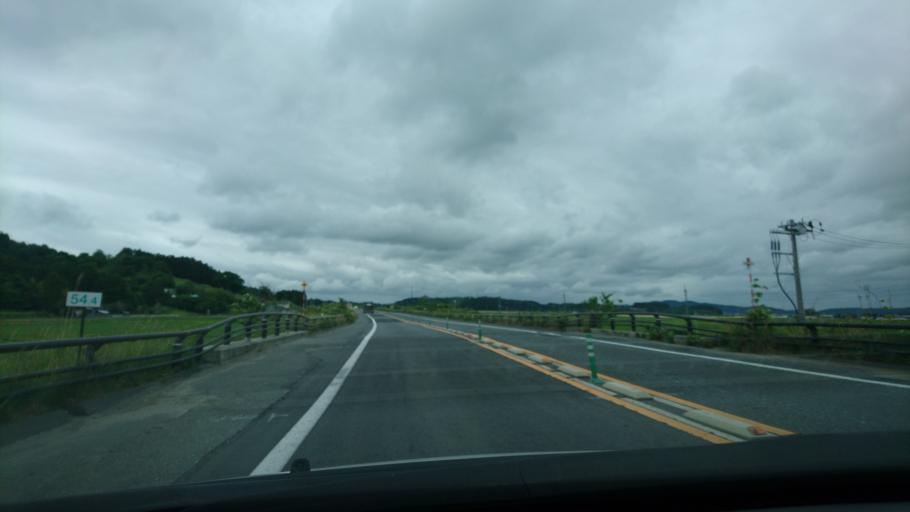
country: JP
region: Miyagi
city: Wakuya
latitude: 38.5848
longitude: 141.2753
